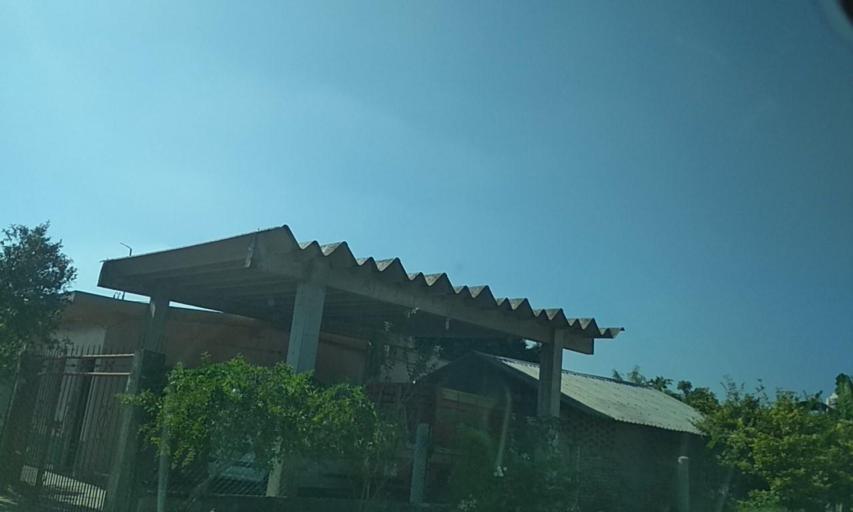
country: MX
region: Veracruz
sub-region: Martinez de la Torre
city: La Union Paso Largo
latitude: 20.1427
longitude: -96.9972
